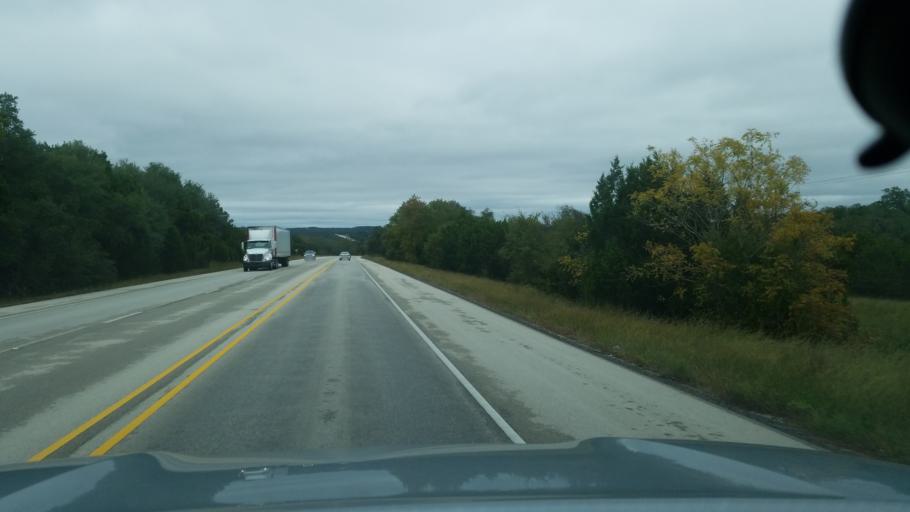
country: US
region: Texas
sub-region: Blanco County
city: Blanco
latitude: 29.9881
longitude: -98.4081
